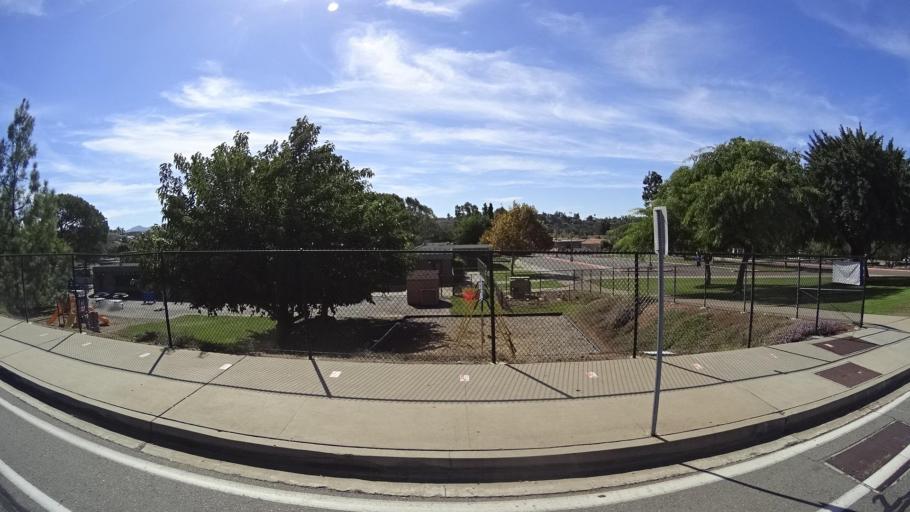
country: US
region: California
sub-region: San Diego County
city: Casa de Oro-Mount Helix
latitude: 32.7513
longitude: -116.9602
